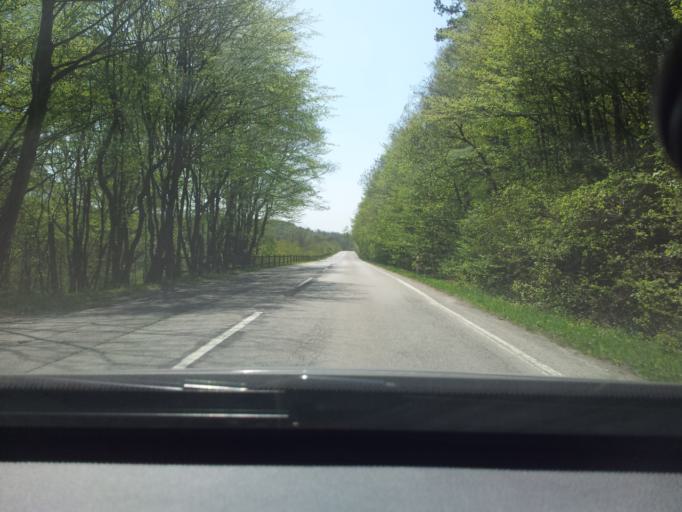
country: SK
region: Nitriansky
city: Zlate Moravce
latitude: 48.4699
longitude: 18.4115
